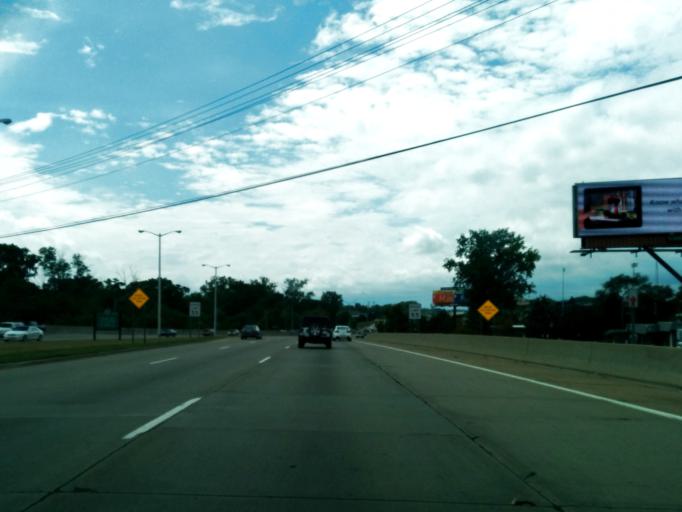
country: US
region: Michigan
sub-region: Macomb County
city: Utica
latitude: 42.6254
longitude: -83.0340
